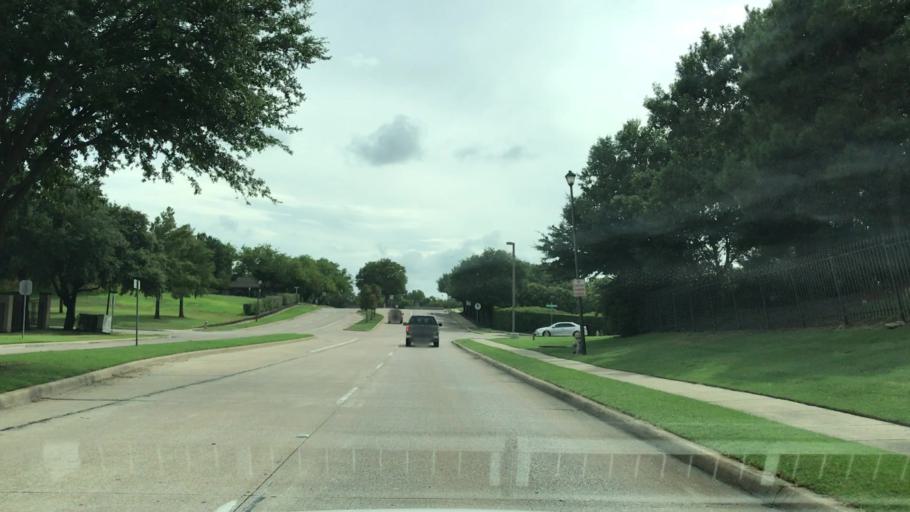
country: US
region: Texas
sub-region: Dallas County
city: Irving
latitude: 32.8600
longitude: -96.9545
